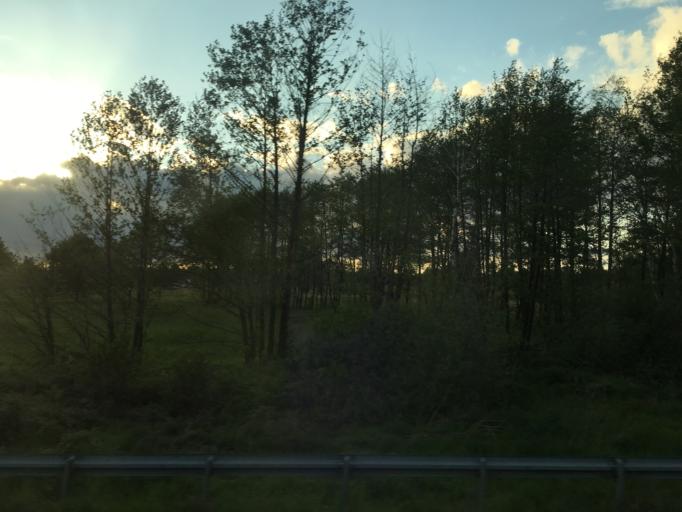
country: DE
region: Brandenburg
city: Hohenleipisch
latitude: 51.4848
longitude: 13.5526
